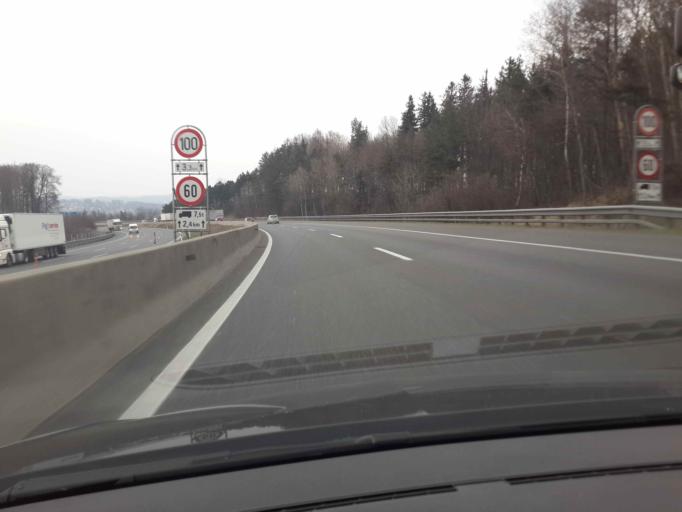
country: AT
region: Lower Austria
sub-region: Politischer Bezirk Sankt Polten
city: Eichgraben
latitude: 48.1438
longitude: 15.9837
